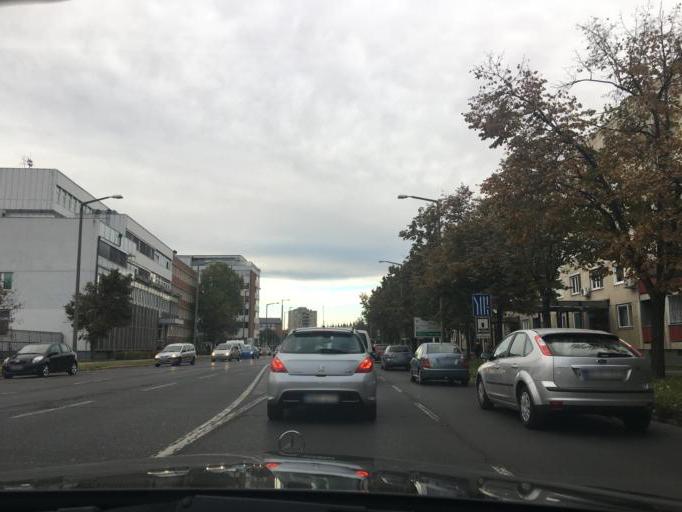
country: HU
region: Hajdu-Bihar
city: Debrecen
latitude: 47.5283
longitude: 21.6318
